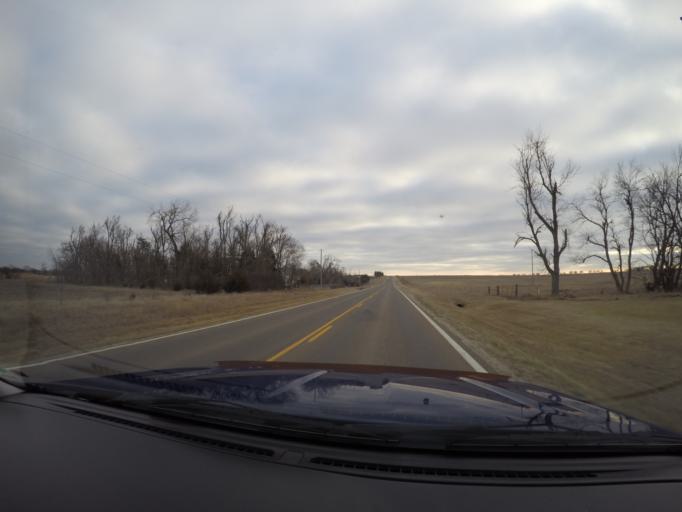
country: US
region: Kansas
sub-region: Morris County
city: Council Grove
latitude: 38.8018
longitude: -96.5013
